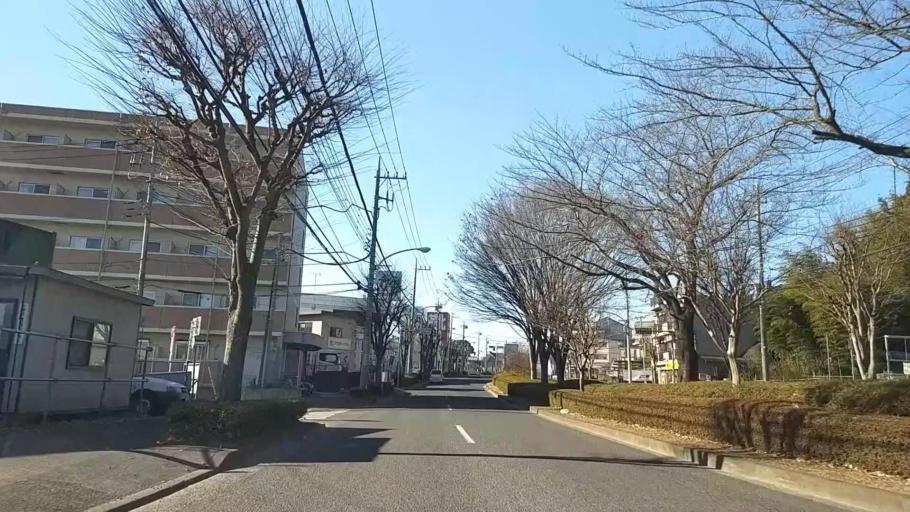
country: JP
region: Tokyo
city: Hino
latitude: 35.6400
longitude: 139.4246
